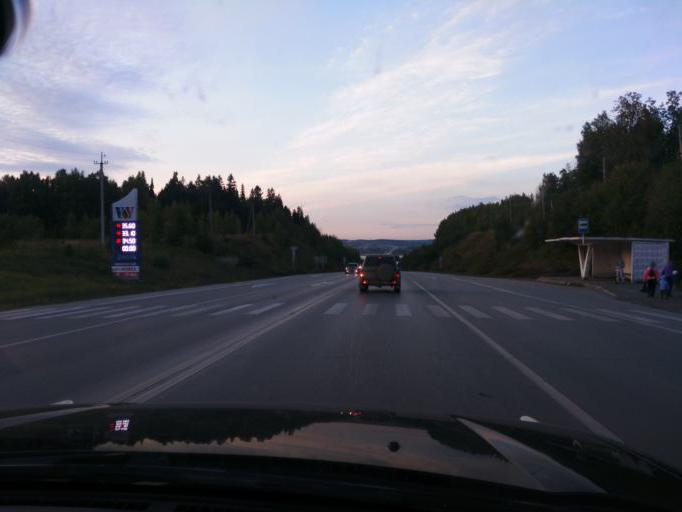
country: RU
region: Perm
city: Polazna
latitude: 58.1497
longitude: 56.4188
